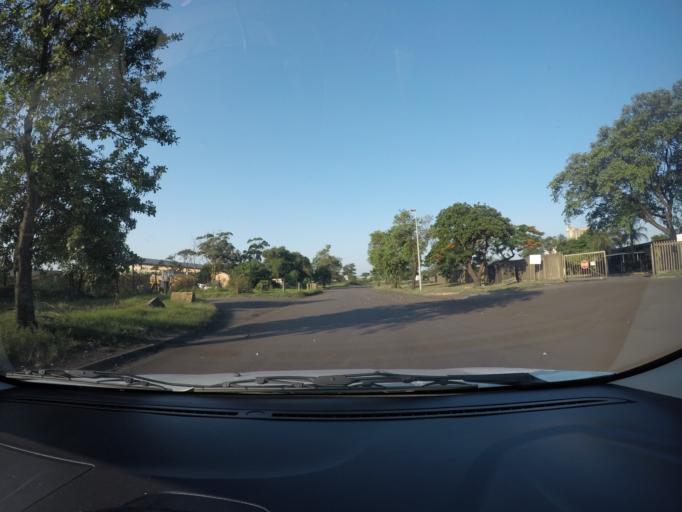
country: ZA
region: KwaZulu-Natal
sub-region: uThungulu District Municipality
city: Richards Bay
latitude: -28.7592
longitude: 32.0090
